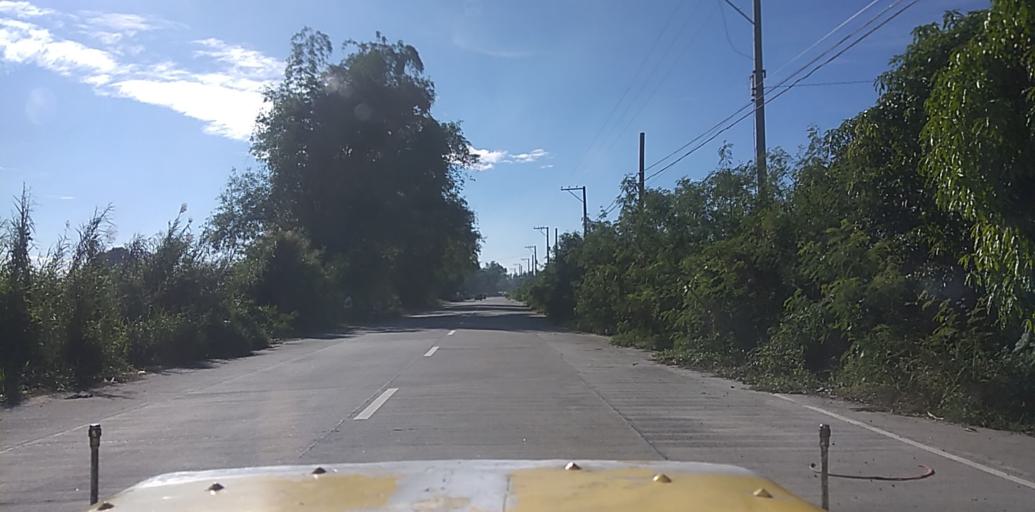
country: PH
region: Central Luzon
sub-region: Province of Pampanga
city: Anao
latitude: 15.1243
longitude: 120.6998
